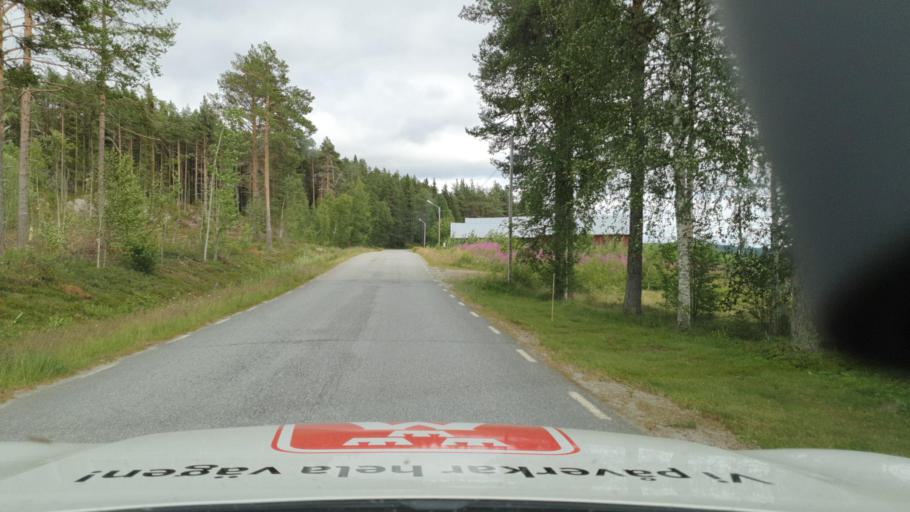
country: SE
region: Vaesterbotten
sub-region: Dorotea Kommun
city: Dorotea
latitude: 64.1901
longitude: 16.6341
